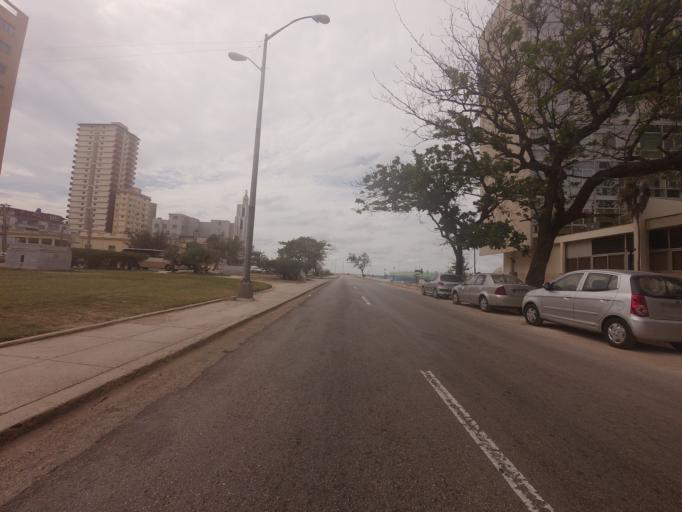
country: CU
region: La Habana
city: Havana
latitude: 23.1435
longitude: -82.3943
